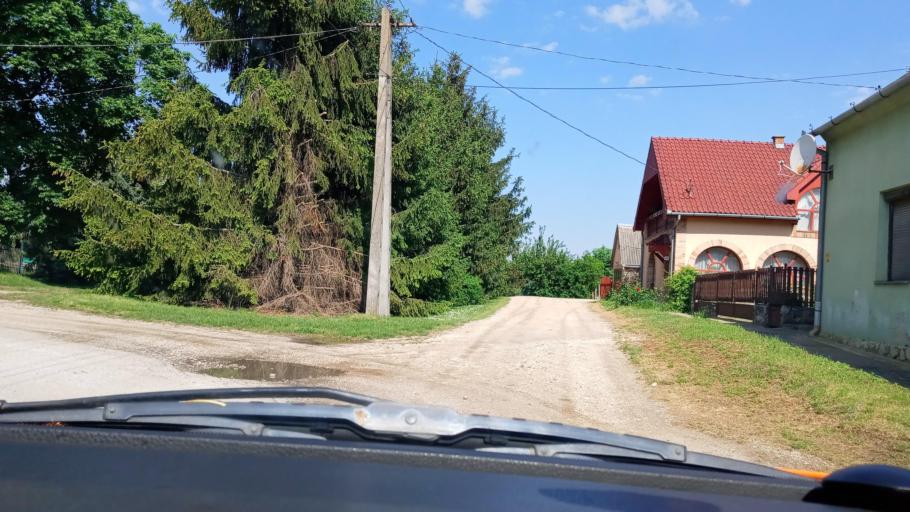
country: HU
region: Baranya
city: Harkany
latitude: 45.9076
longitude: 18.2581
